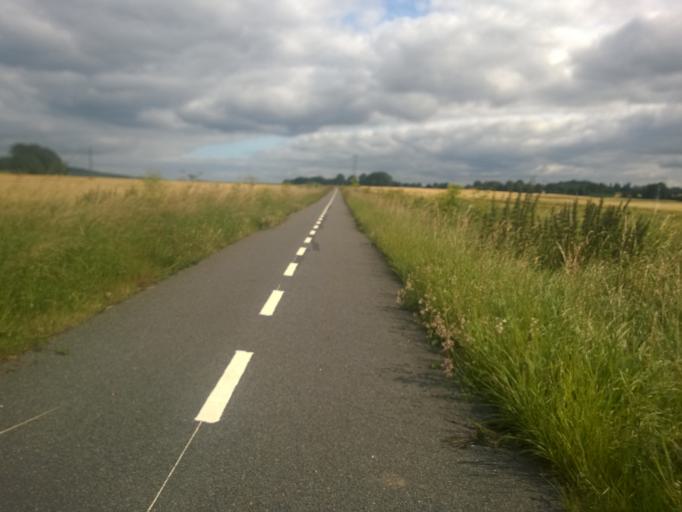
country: SE
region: Skane
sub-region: Kristianstads Kommun
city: Kristianstad
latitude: 56.0668
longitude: 14.1922
